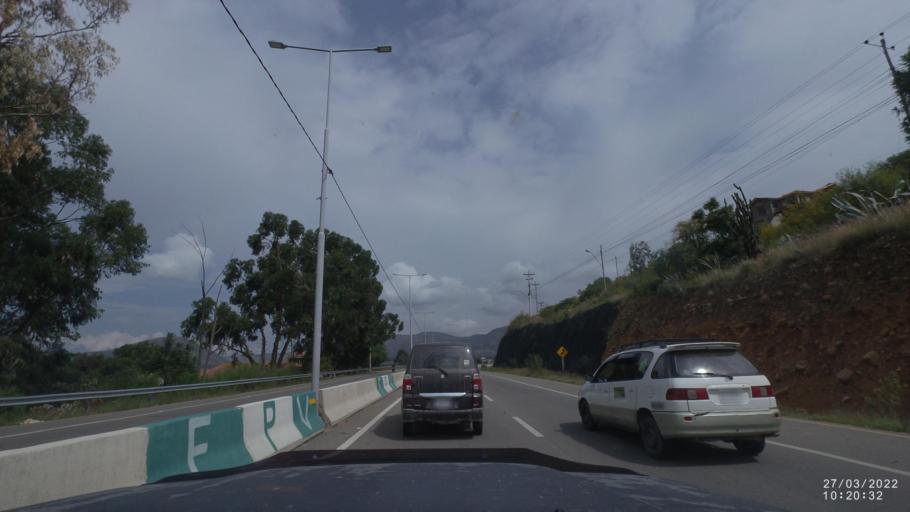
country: BO
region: Cochabamba
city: Tarata
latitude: -17.5356
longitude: -66.0794
